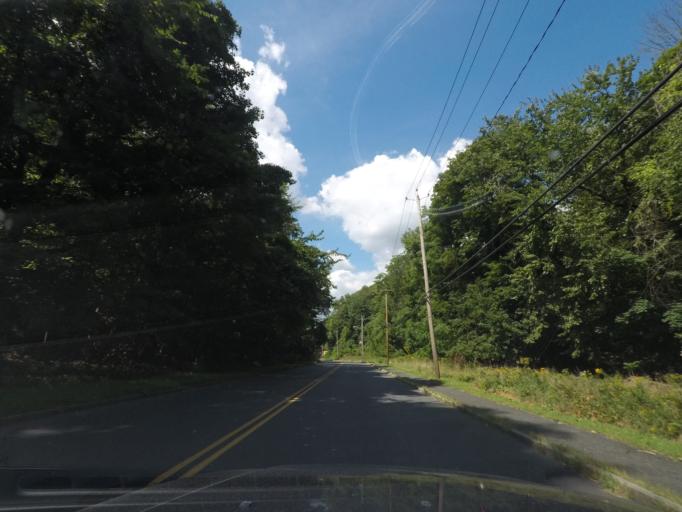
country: US
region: New York
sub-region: Rensselaer County
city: Troy
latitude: 42.7154
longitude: -73.6737
